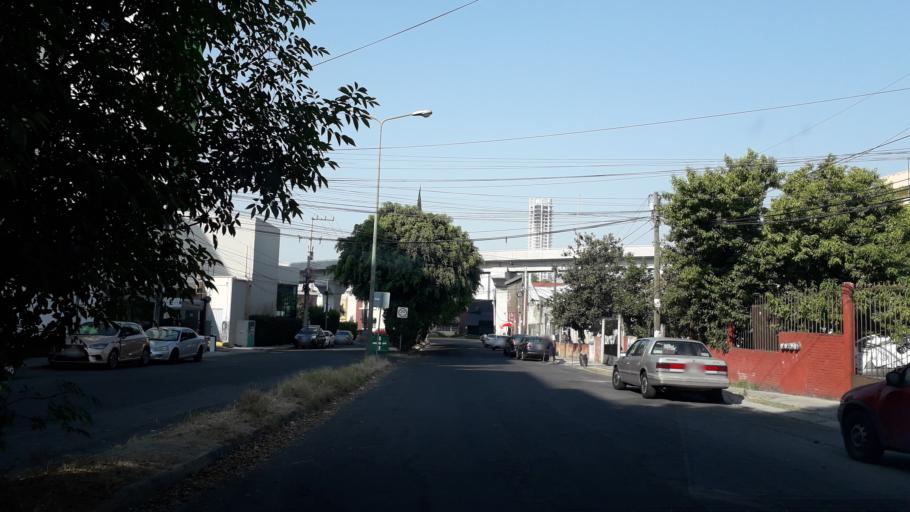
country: MX
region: Puebla
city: Puebla
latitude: 19.0361
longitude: -98.2239
